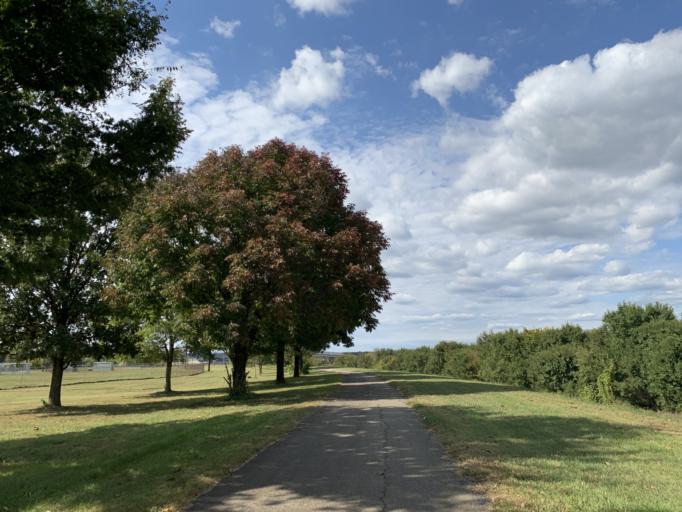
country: US
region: Kentucky
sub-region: Jefferson County
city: Louisville
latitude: 38.2739
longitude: -85.7838
